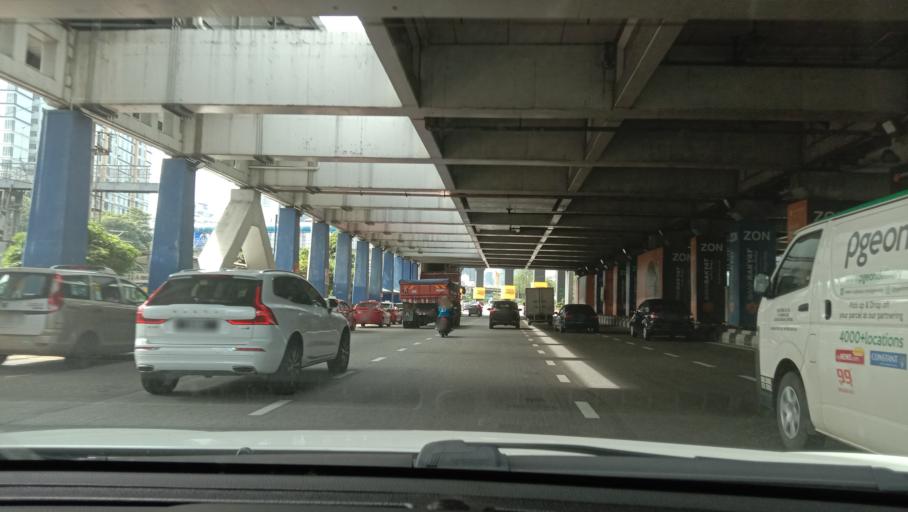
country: MY
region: Kuala Lumpur
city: Kuala Lumpur
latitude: 3.1279
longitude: 101.6794
